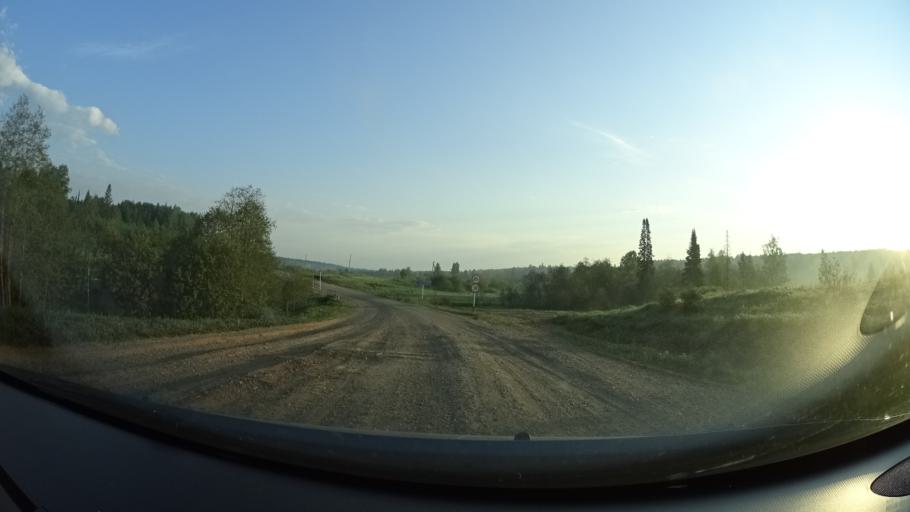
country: RU
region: Perm
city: Kuyeda
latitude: 56.6082
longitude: 55.7134
